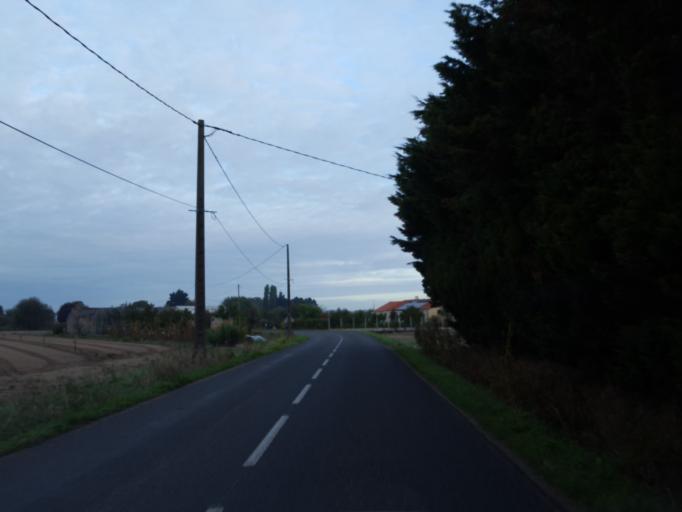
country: FR
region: Pays de la Loire
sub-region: Departement de la Loire-Atlantique
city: Saint-Julien-de-Concelles
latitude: 47.2419
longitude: -1.3928
